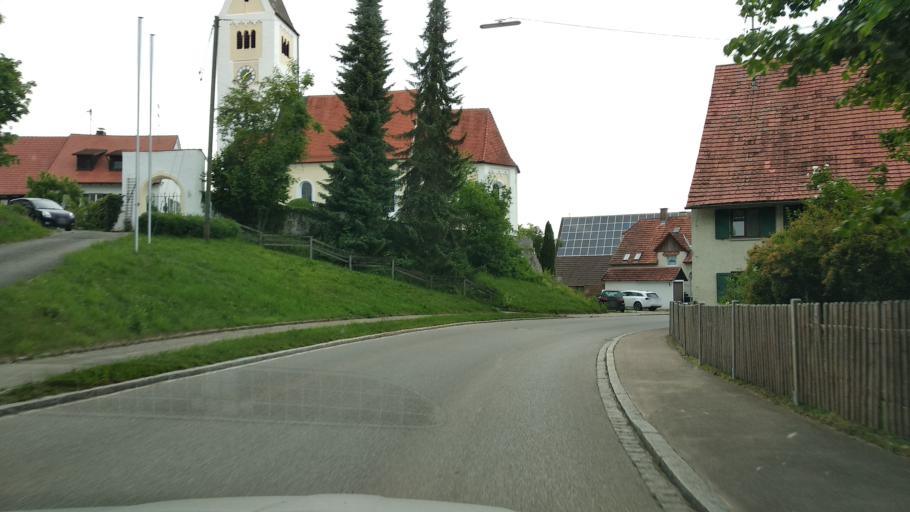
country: DE
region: Bavaria
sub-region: Swabia
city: Lachen
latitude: 47.9525
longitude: 10.2248
